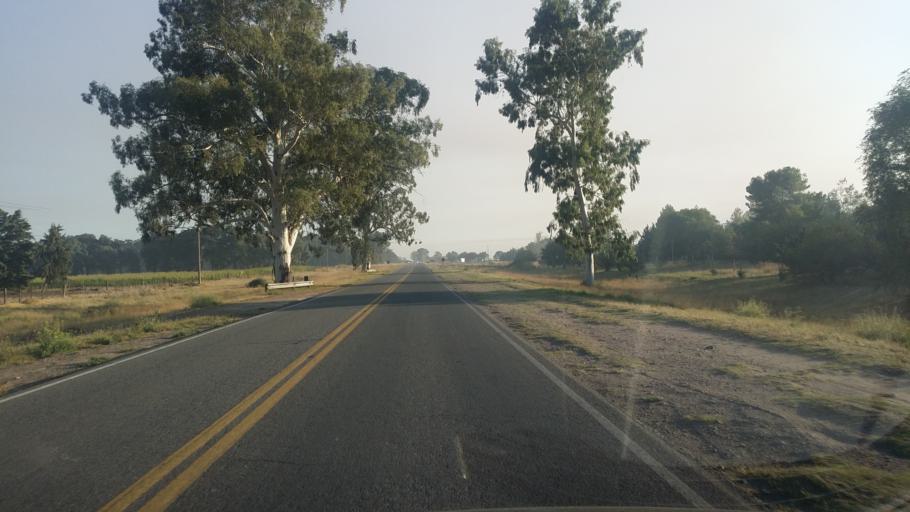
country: AR
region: La Pampa
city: Santa Rosa
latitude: -36.5774
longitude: -64.2811
